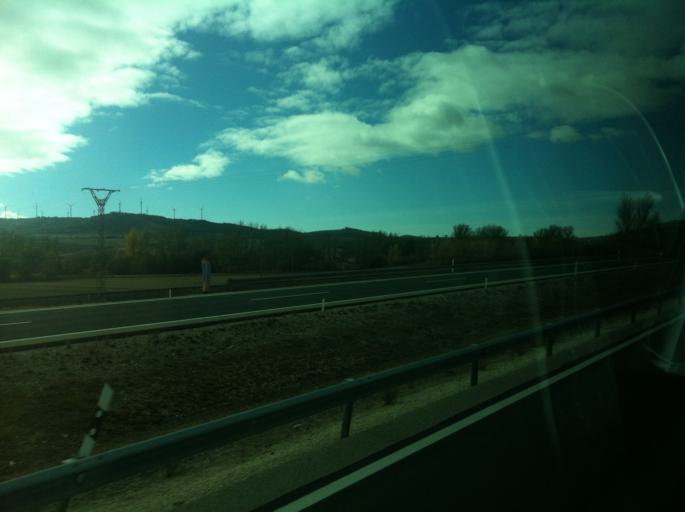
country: ES
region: Castille and Leon
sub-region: Provincia de Burgos
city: Castil de Peones
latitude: 42.4841
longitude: -3.3993
